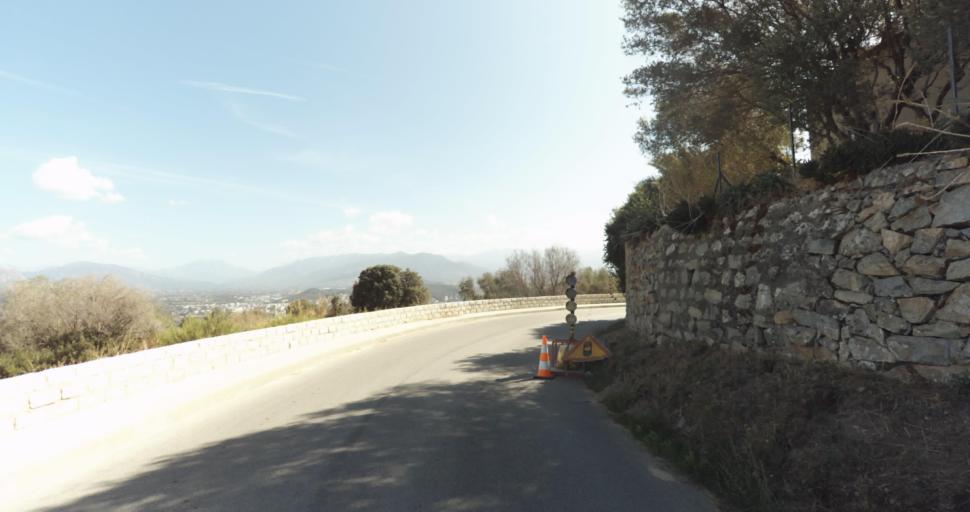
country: FR
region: Corsica
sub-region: Departement de la Corse-du-Sud
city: Ajaccio
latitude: 41.9260
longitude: 8.7178
